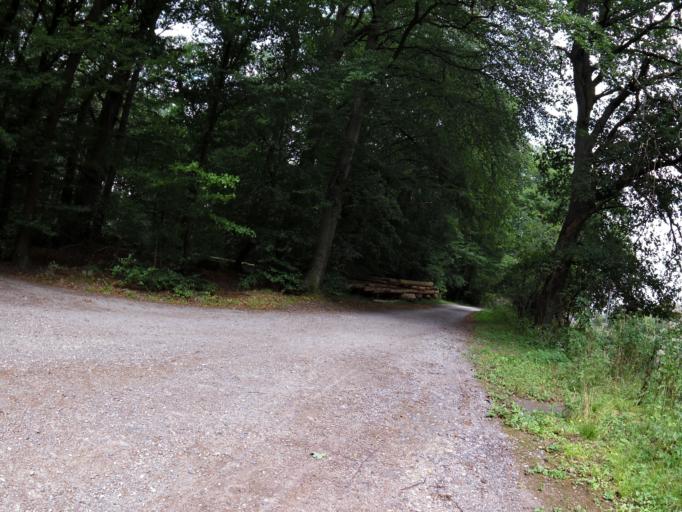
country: DE
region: North Rhine-Westphalia
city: Stolberg
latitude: 50.7457
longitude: 6.2910
